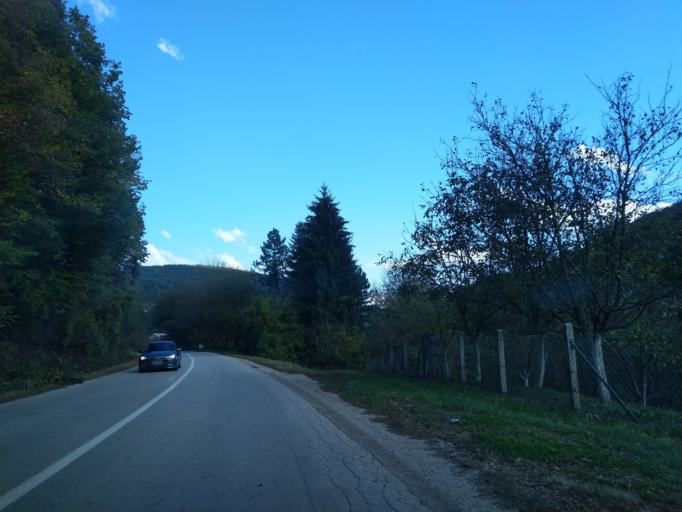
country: RS
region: Central Serbia
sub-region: Zlatiborski Okrug
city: Uzice
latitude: 43.8793
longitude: 19.7836
